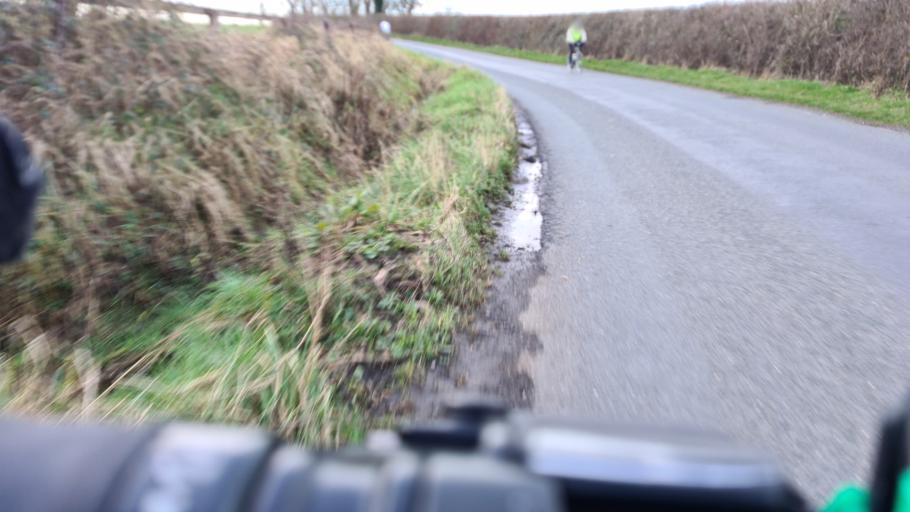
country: IE
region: Leinster
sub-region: Kildare
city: Celbridge
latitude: 53.3458
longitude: -6.5667
